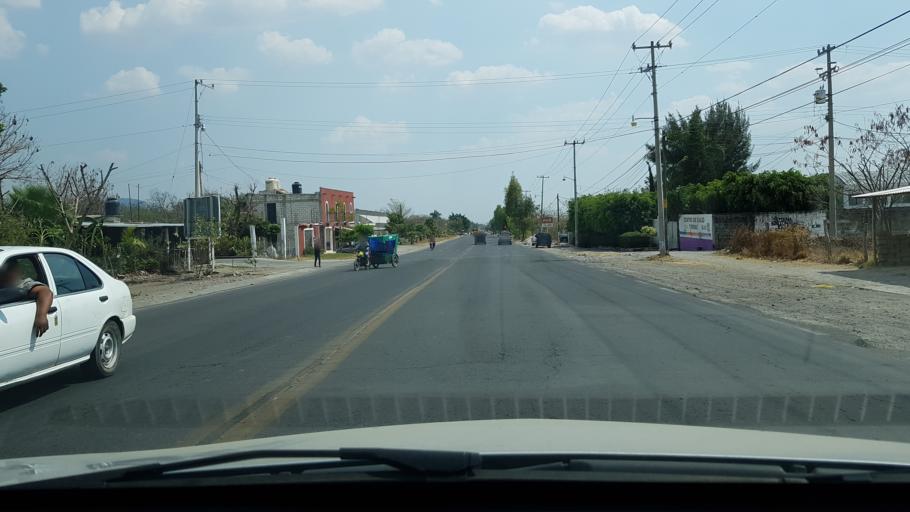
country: MX
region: Morelos
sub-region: Temoac
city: Temoac
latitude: 18.7683
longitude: -98.7790
